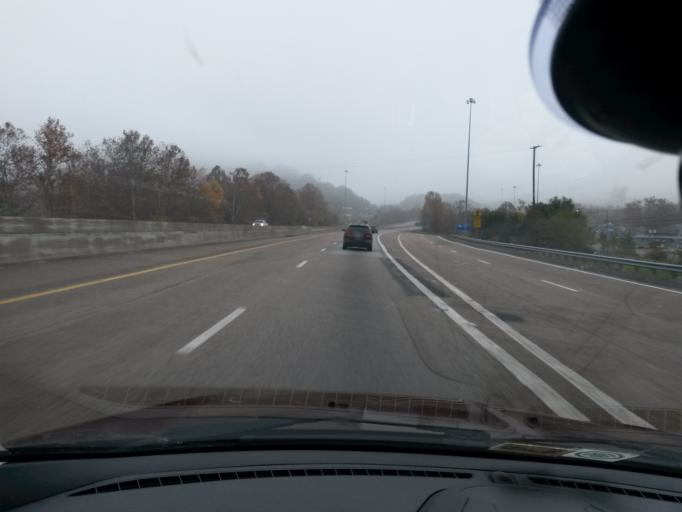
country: US
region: Virginia
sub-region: City of Covington
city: Fairlawn
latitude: 37.7723
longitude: -79.9627
